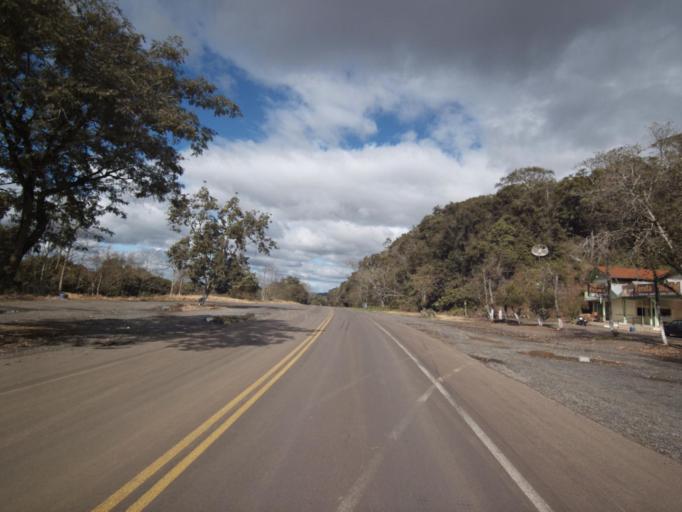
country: BR
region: Santa Catarina
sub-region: Concordia
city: Concordia
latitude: -27.3425
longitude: -51.9859
